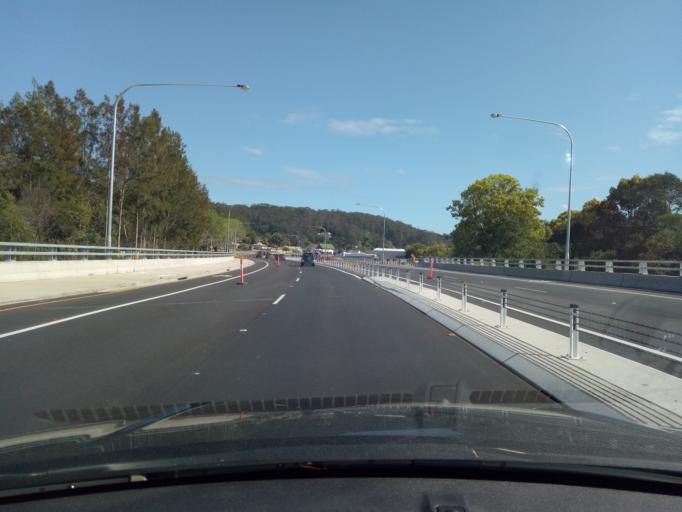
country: AU
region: New South Wales
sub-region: Gosford Shire
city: Lisarow
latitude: -33.3669
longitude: 151.3745
